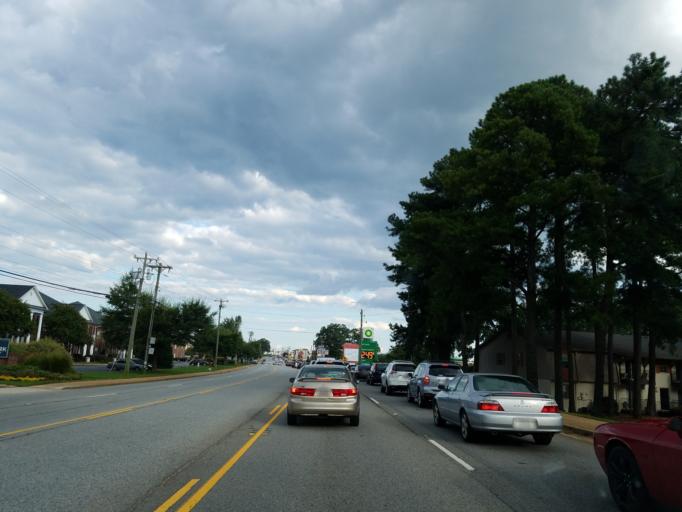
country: US
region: South Carolina
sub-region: Greenville County
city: Taylors
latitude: 34.8610
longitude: -82.2733
